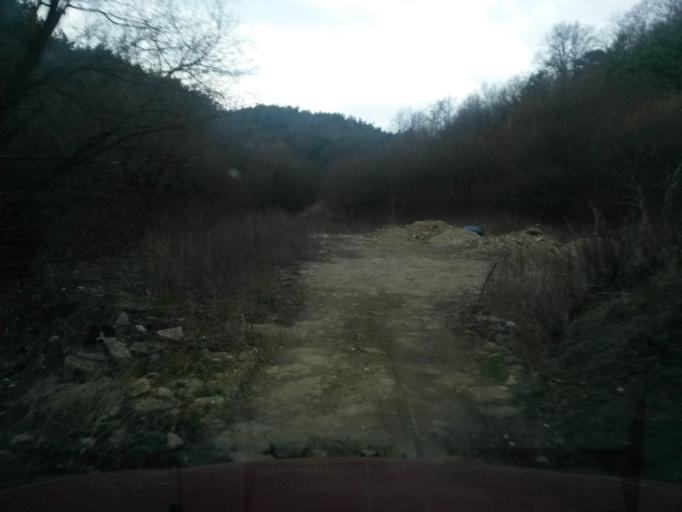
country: SK
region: Kosicky
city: Kosice
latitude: 48.7627
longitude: 21.2569
